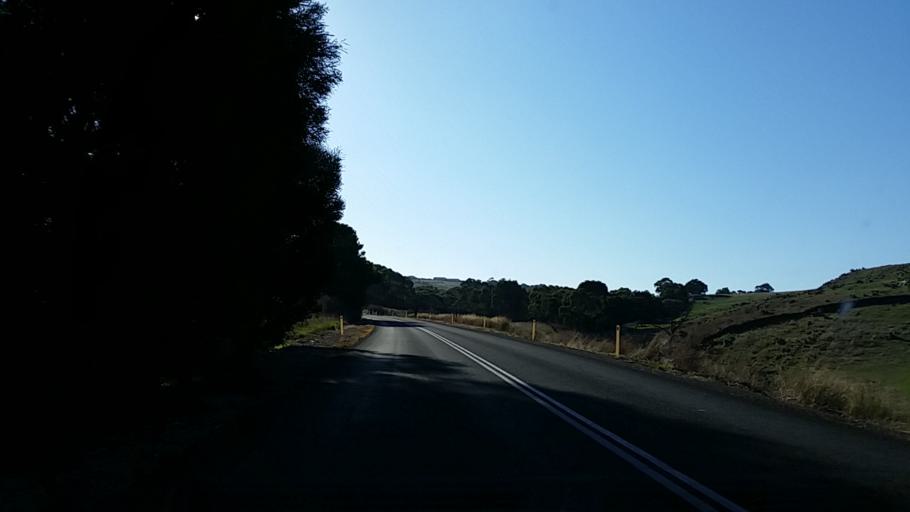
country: AU
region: South Australia
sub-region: Alexandrina
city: Strathalbyn
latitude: -35.1808
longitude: 138.9473
